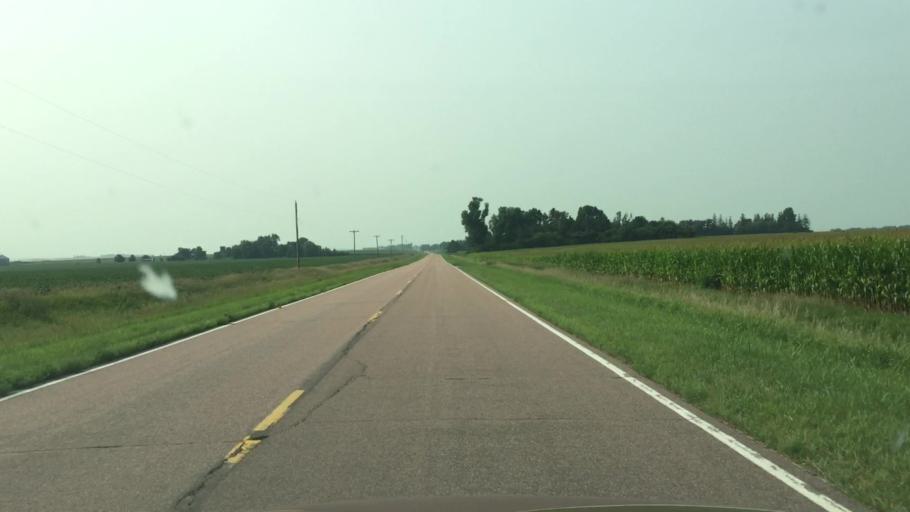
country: US
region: Iowa
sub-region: O'Brien County
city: Sheldon
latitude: 43.2523
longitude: -95.7832
